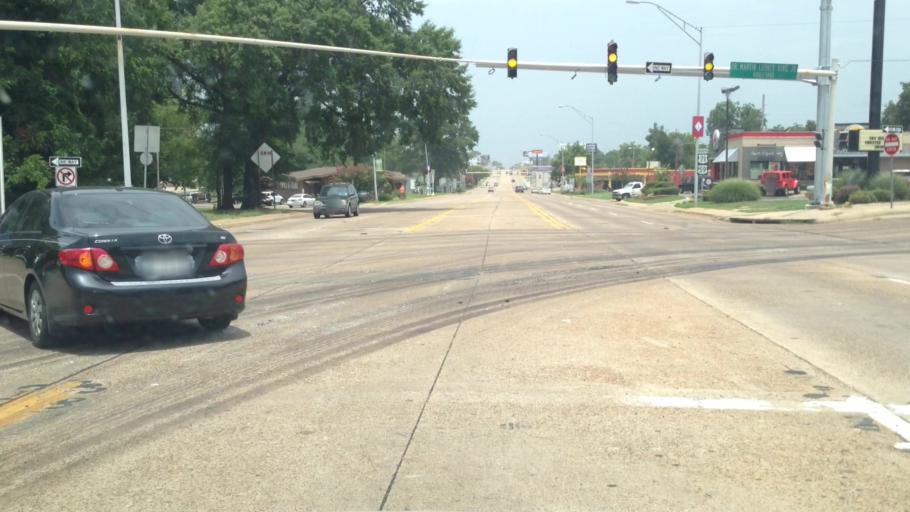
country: US
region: Texas
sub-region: Bowie County
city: Texarkana
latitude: 33.4282
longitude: -94.0431
